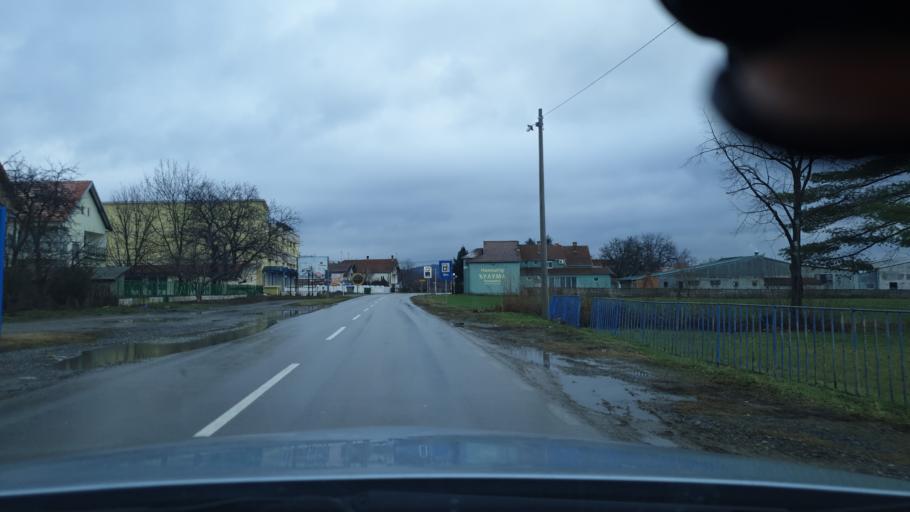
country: RS
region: Central Serbia
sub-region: Branicevski Okrug
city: Petrovac
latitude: 44.4040
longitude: 21.3978
